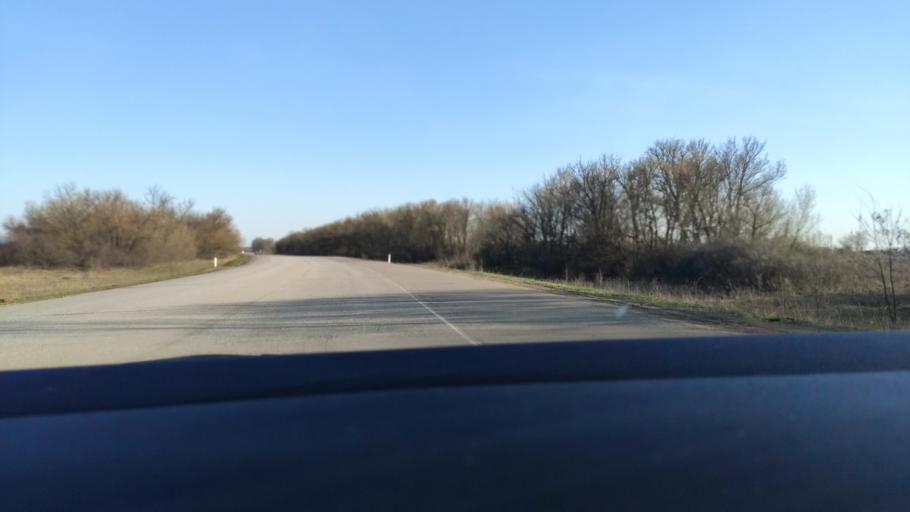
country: RU
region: Voronezj
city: Kolodeznyy
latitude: 51.3151
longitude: 39.0284
